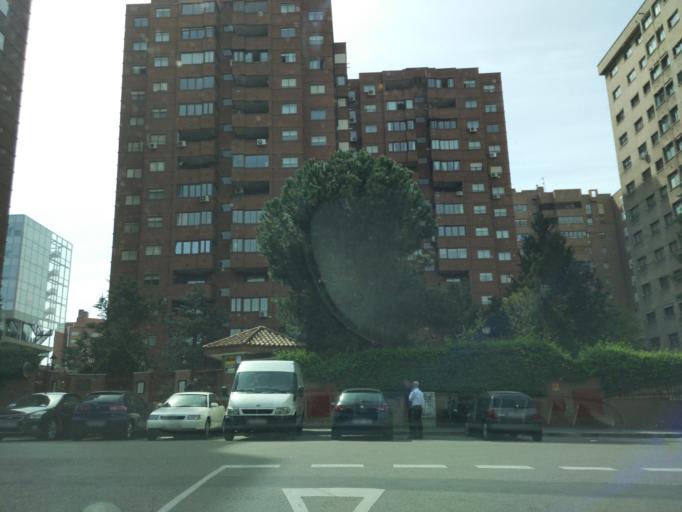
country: ES
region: Madrid
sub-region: Provincia de Madrid
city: Tetuan de las Victorias
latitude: 40.4780
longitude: -3.6969
